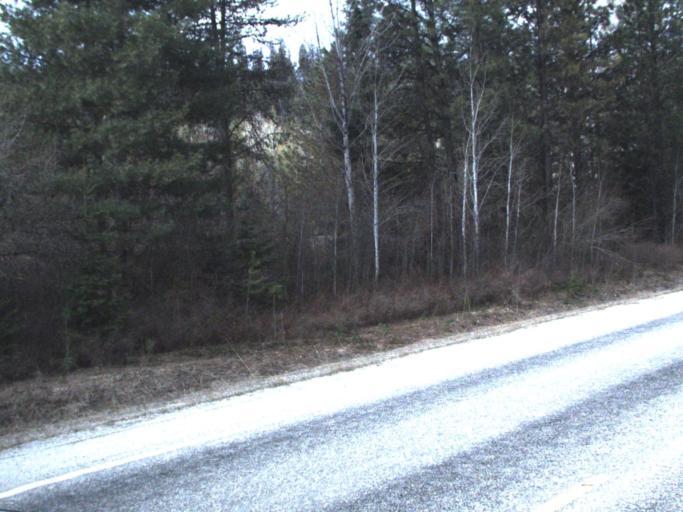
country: US
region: Washington
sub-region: Stevens County
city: Chewelah
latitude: 48.5504
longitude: -117.3350
